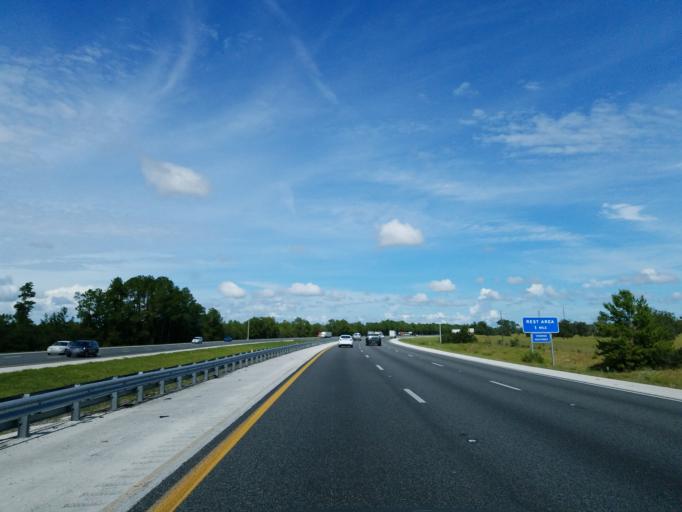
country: US
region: Florida
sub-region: Marion County
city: Ocala
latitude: 29.0754
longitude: -82.1832
